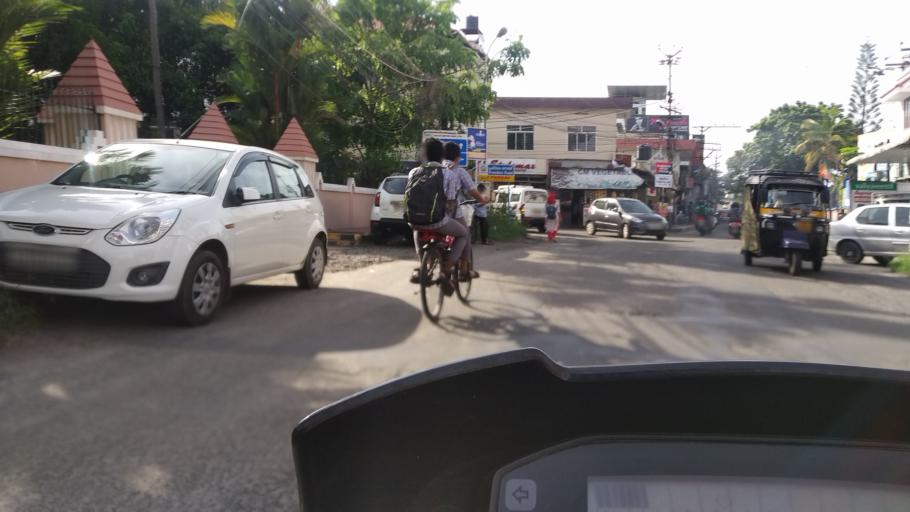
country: IN
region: Kerala
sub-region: Ernakulam
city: Elur
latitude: 10.0021
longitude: 76.2957
